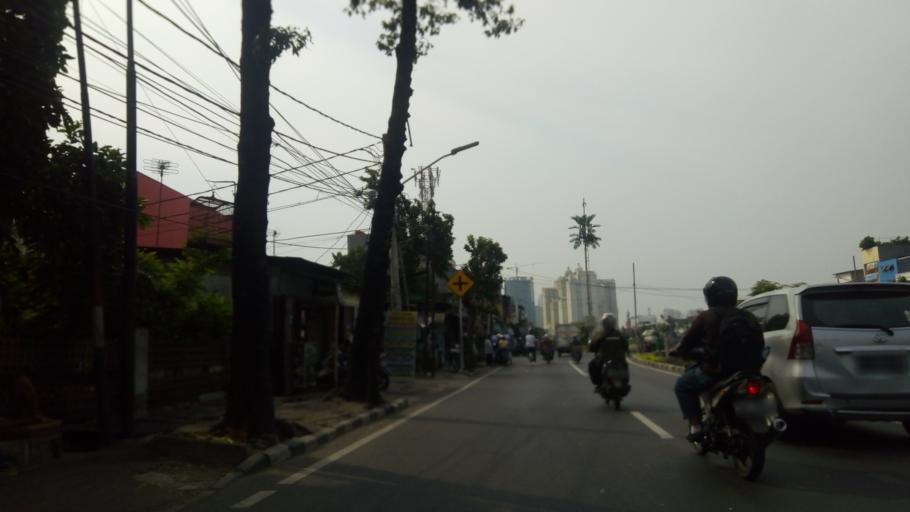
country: ID
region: Jakarta Raya
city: Jakarta
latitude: -6.1697
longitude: 106.8519
